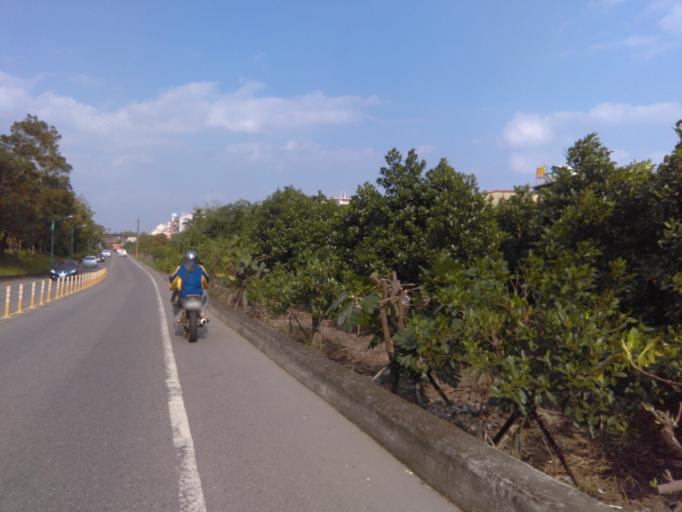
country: TW
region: Taiwan
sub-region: Yilan
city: Yilan
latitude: 24.7590
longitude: 121.7466
